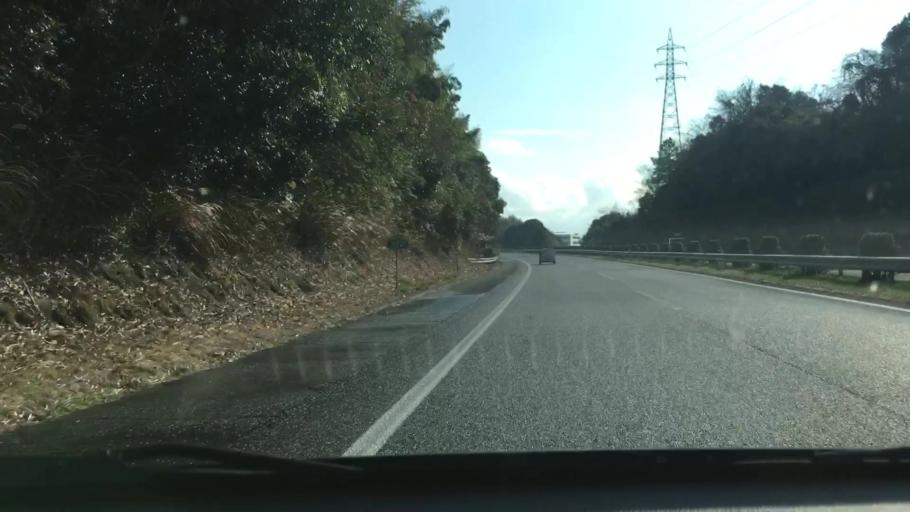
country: JP
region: Kumamoto
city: Matsubase
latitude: 32.6329
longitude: 130.7102
